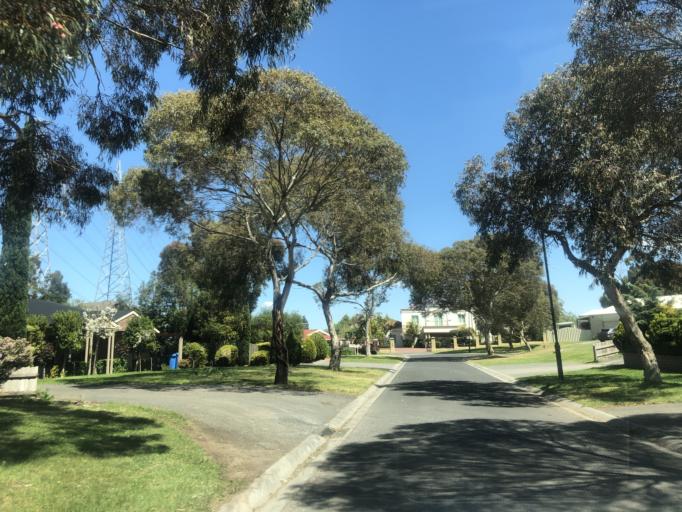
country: AU
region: Victoria
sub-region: Casey
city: Narre Warren North
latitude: -37.9921
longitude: 145.2865
